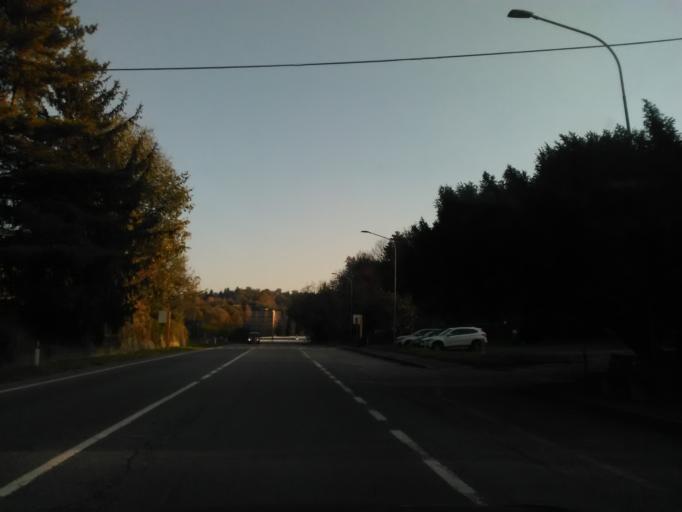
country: IT
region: Piedmont
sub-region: Provincia di Torino
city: Banchette
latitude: 45.4557
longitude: 7.8598
